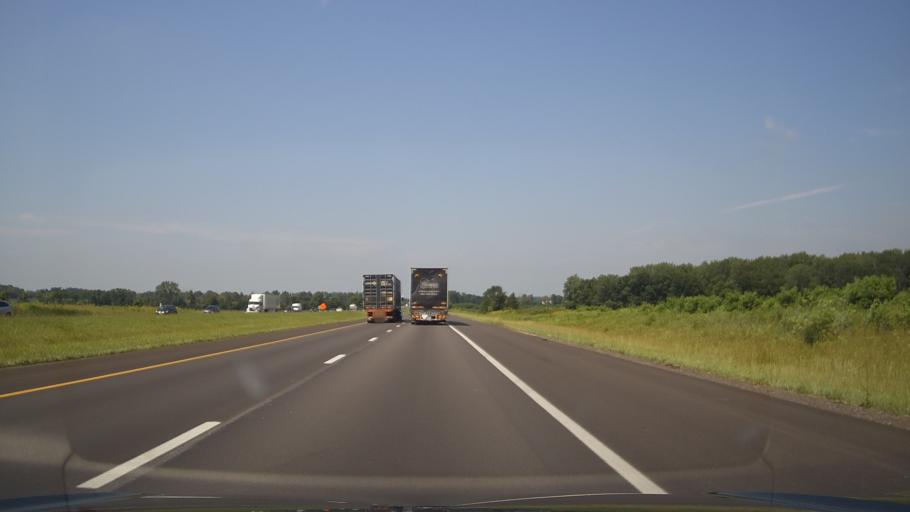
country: US
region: Ohio
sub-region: Warren County
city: Waynesville
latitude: 39.4551
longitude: -84.0043
